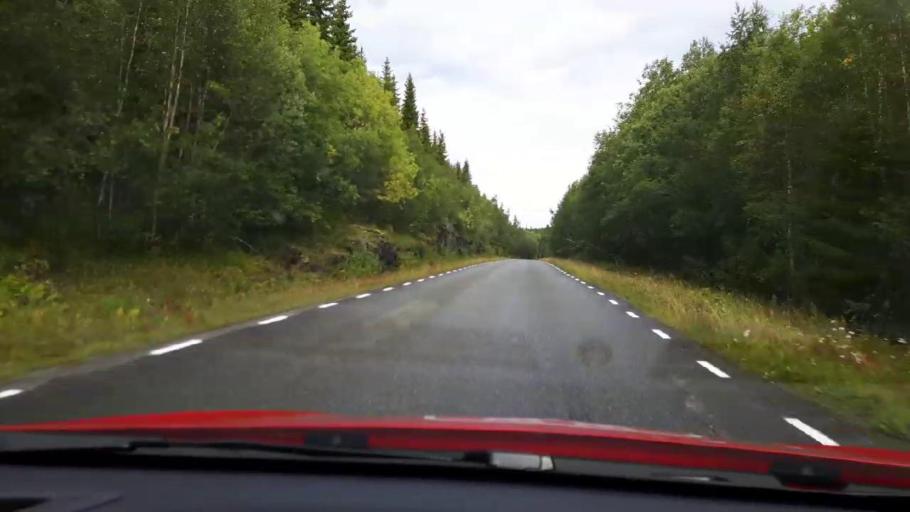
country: SE
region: Jaemtland
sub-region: Are Kommun
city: Are
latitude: 63.7236
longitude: 12.9693
